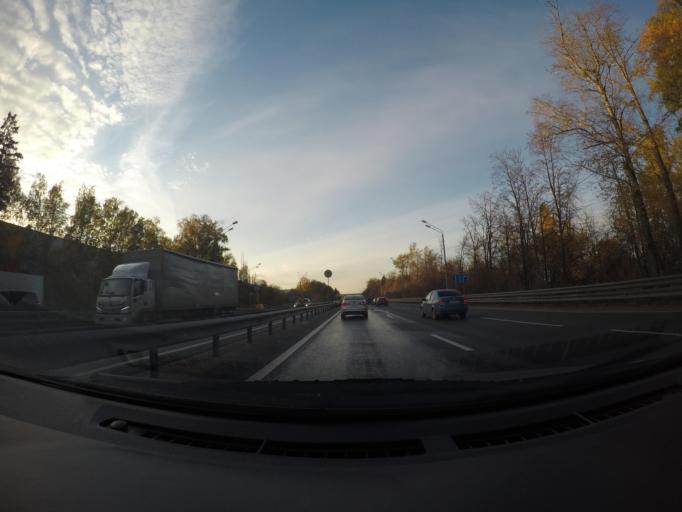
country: RU
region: Moskovskaya
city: Skhodnya
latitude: 55.9808
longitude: 37.2931
